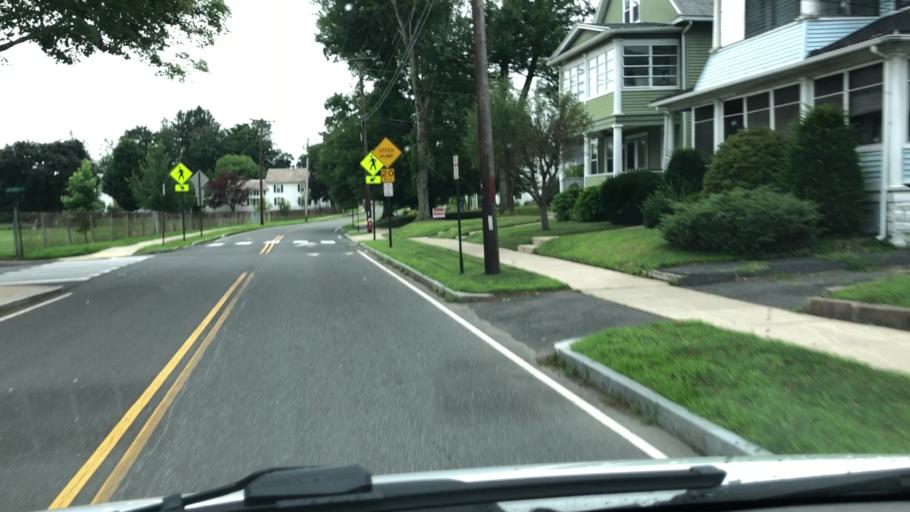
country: US
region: Massachusetts
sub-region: Hampshire County
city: Northampton
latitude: 42.3285
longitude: -72.6284
